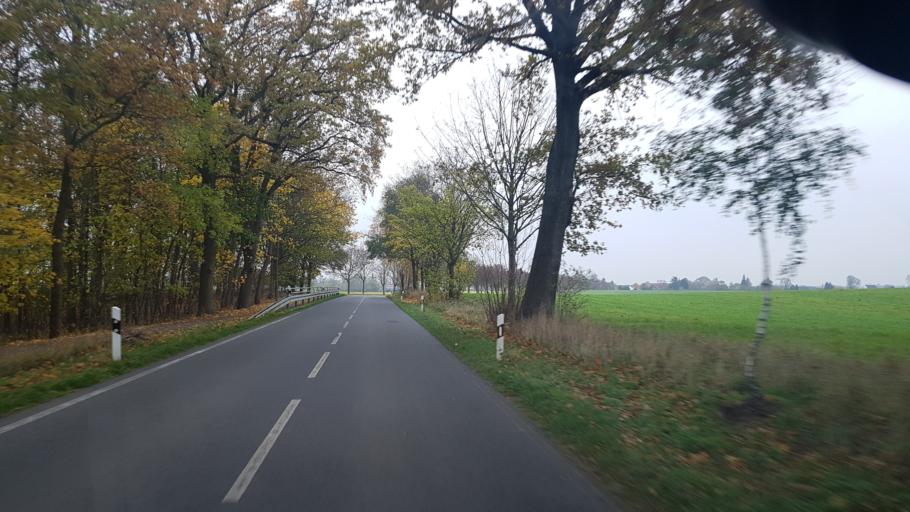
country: DE
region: Brandenburg
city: Schonermark
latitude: 52.9241
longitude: 13.1177
